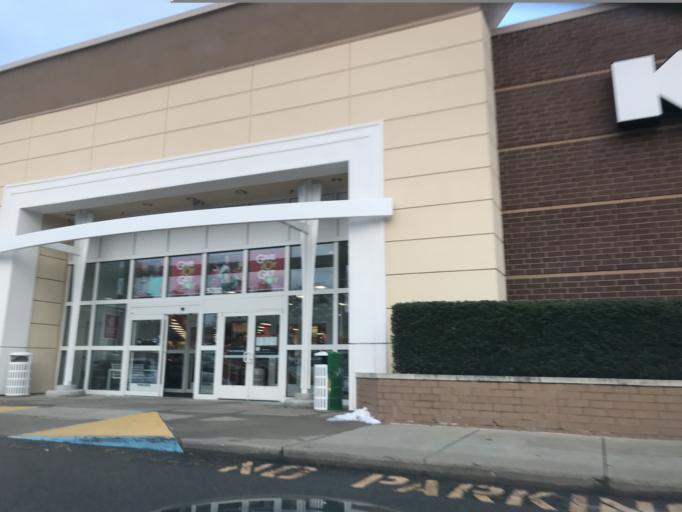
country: US
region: North Carolina
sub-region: Wake County
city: Wake Forest
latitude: 35.9067
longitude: -78.6002
